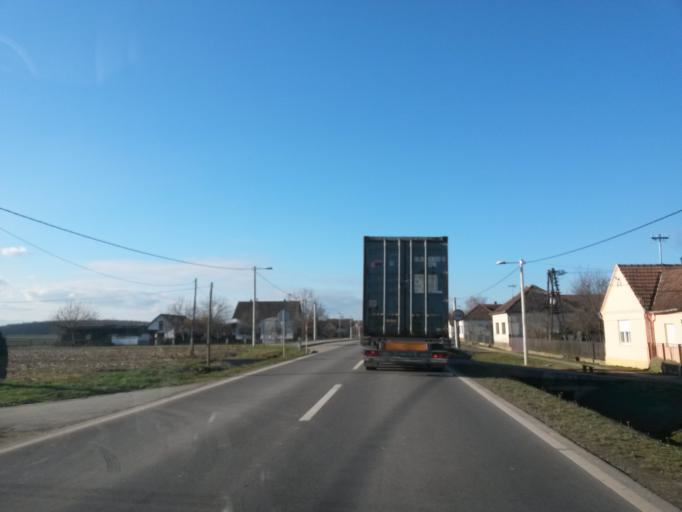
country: HU
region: Baranya
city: Sellye
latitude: 45.7441
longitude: 17.8311
